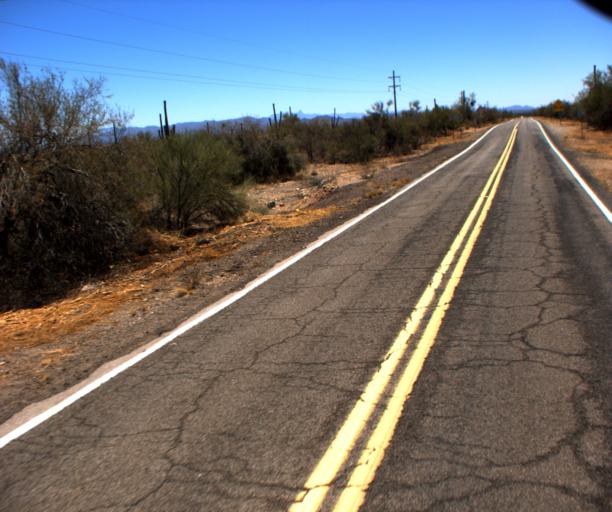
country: US
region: Arizona
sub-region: Pima County
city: Sells
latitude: 32.1507
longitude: -112.1049
